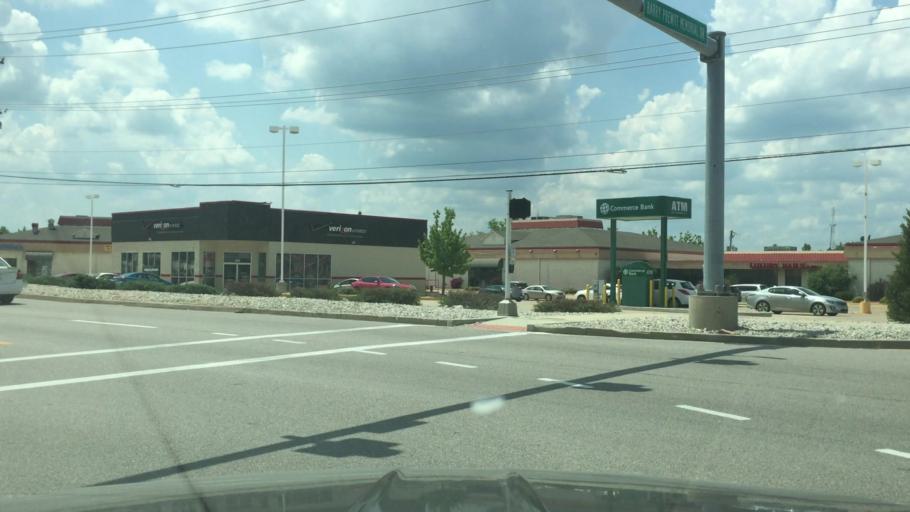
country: US
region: Missouri
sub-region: Miller County
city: Lake Ozark
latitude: 38.1616
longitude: -92.6075
